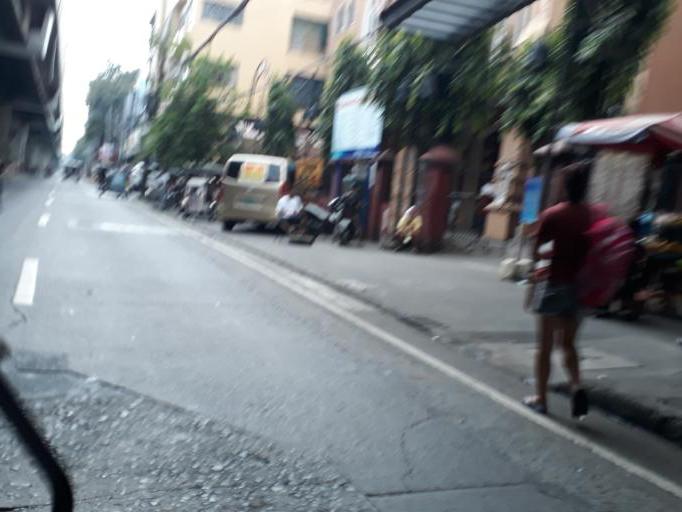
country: PH
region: Metro Manila
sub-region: City of Manila
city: Manila
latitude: 14.6167
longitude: 120.9829
